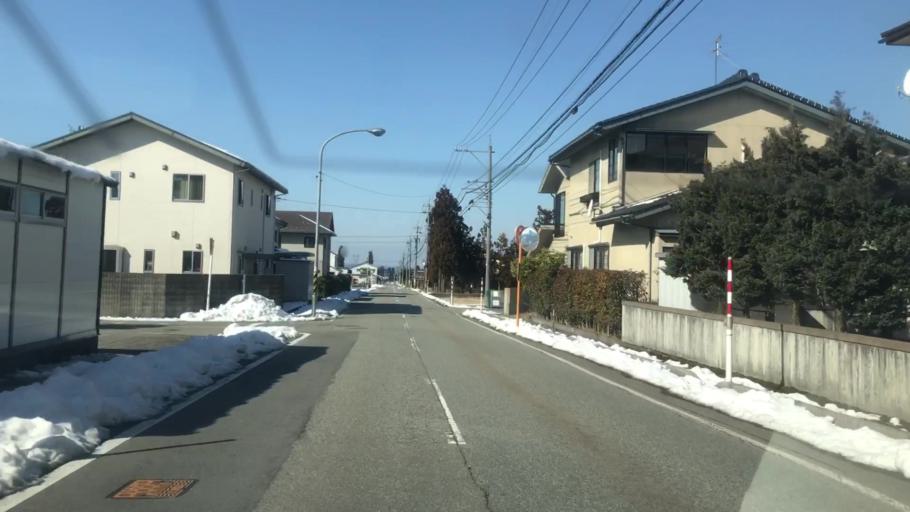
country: JP
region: Toyama
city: Toyama-shi
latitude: 36.6244
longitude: 137.2793
